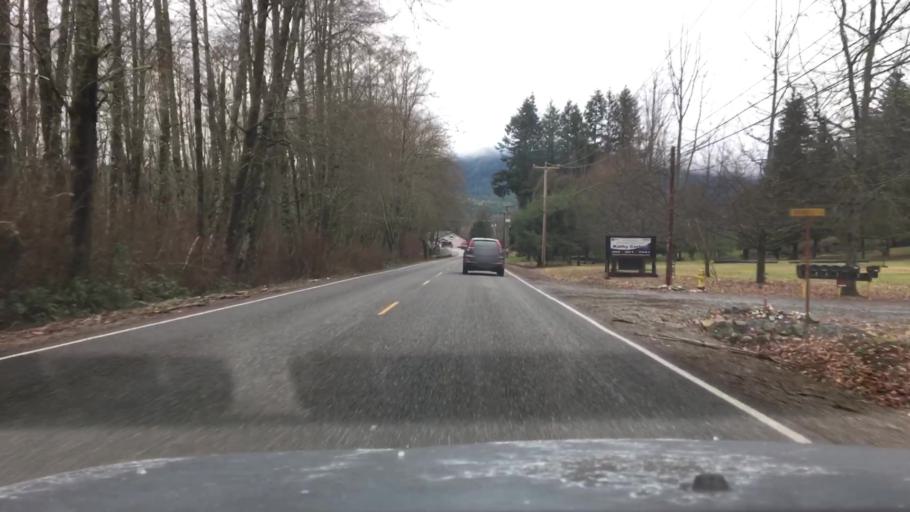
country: US
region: Washington
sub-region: Whatcom County
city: Sudden Valley
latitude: 48.6201
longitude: -122.3358
